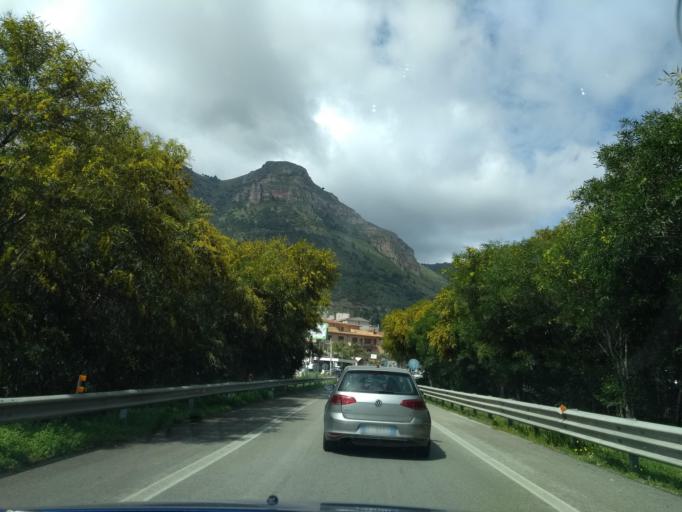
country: IT
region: Sicily
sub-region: Trapani
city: Castellammare del Golfo
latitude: 38.0159
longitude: 12.8930
